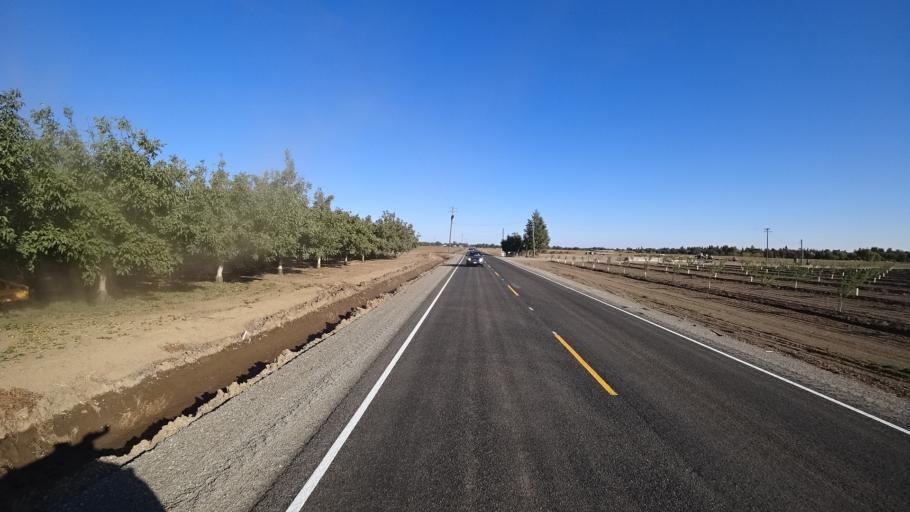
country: US
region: California
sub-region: Yolo County
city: Davis
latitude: 38.5826
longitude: -121.7859
